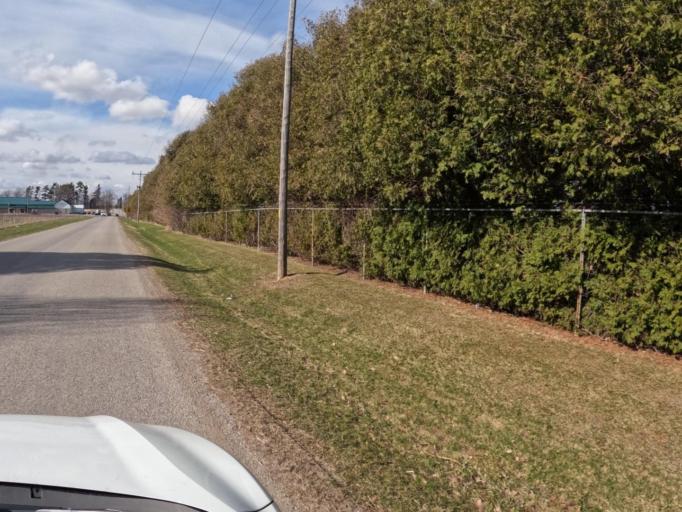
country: CA
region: Ontario
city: Norfolk County
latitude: 42.8613
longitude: -80.2742
